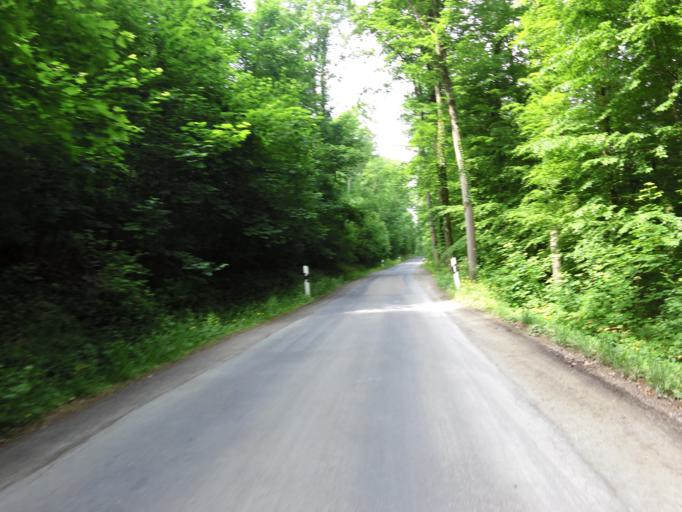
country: DE
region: Bavaria
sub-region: Regierungsbezirk Unterfranken
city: Wuerzburg
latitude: 49.7681
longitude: 9.8805
